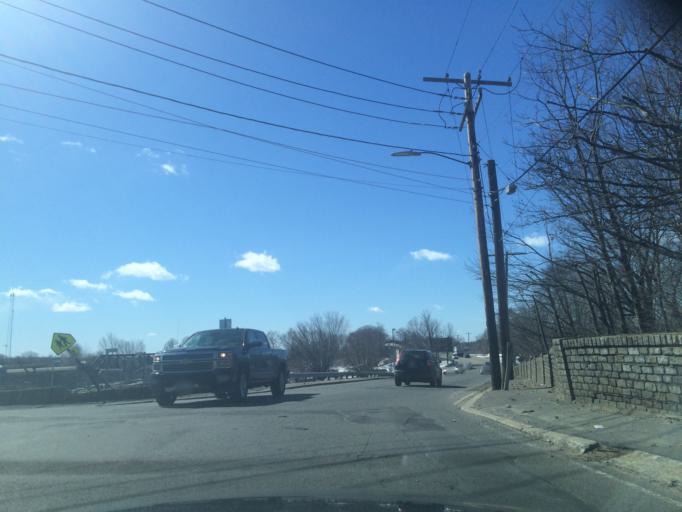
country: US
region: Massachusetts
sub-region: Norfolk County
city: Dedham
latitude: 42.2398
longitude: -71.1338
